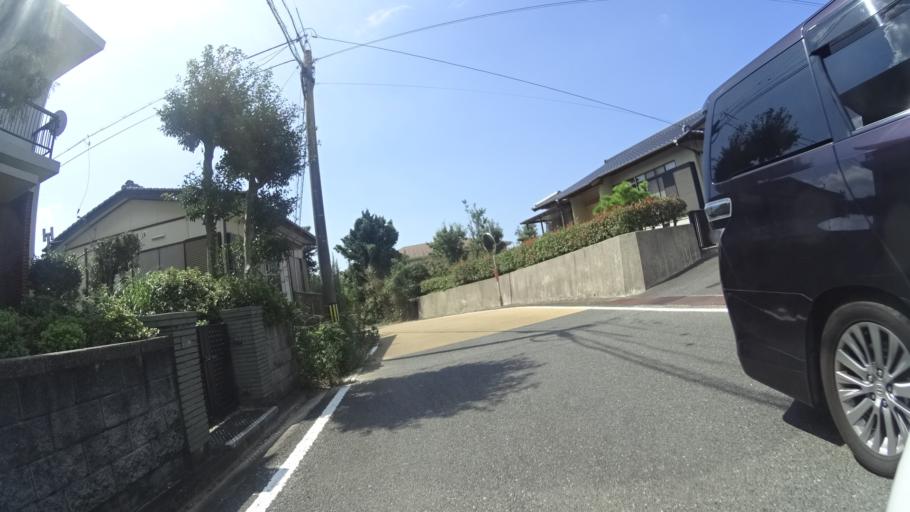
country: JP
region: Yamaguchi
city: Shimonoseki
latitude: 34.0902
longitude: 130.8821
